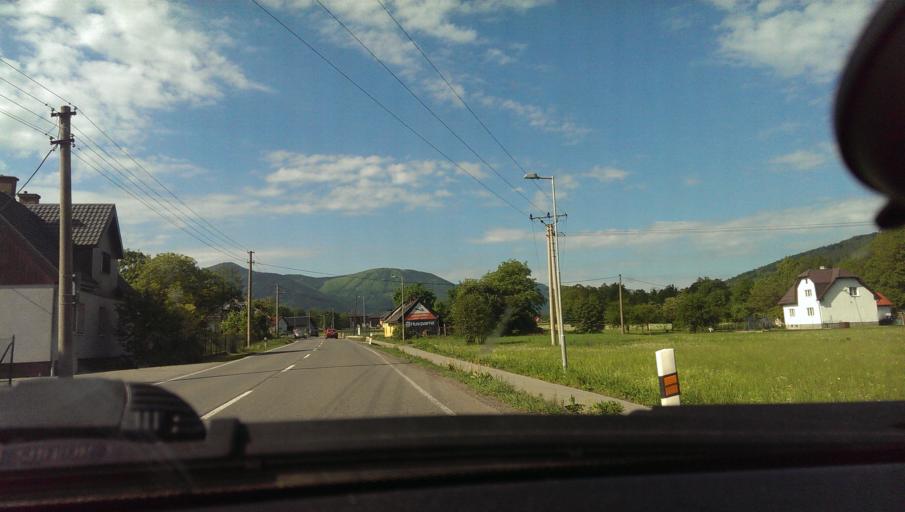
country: CZ
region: Moravskoslezsky
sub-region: Okres Frydek-Mistek
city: Celadna
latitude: 49.5575
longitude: 18.3456
